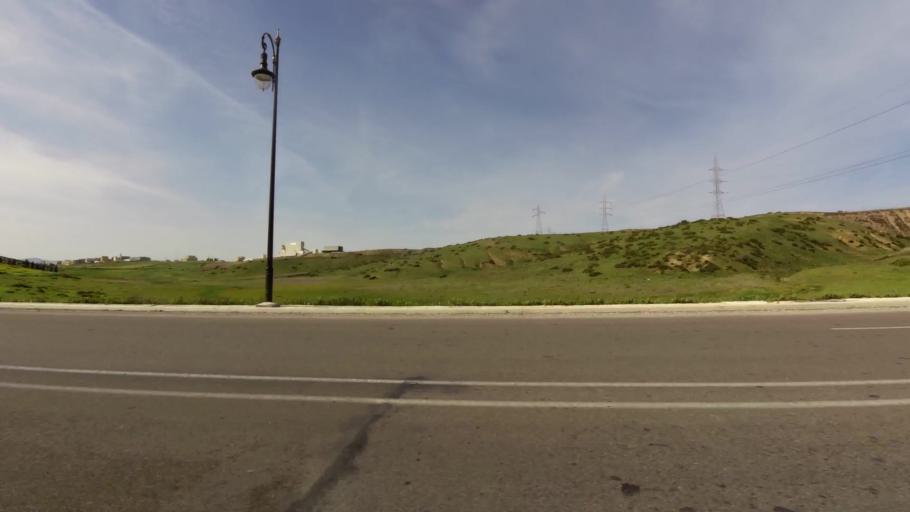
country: MA
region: Tanger-Tetouan
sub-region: Tanger-Assilah
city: Tangier
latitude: 35.7036
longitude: -5.7881
